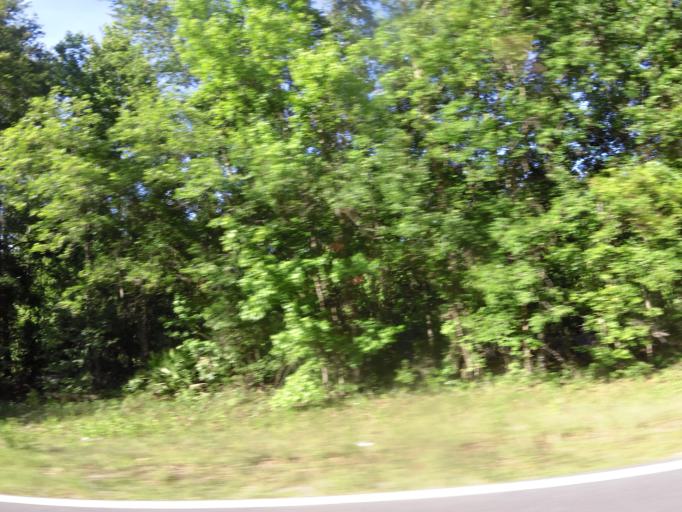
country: US
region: Florida
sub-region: Nassau County
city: Nassau Village-Ratliff
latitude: 30.4801
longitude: -81.8445
